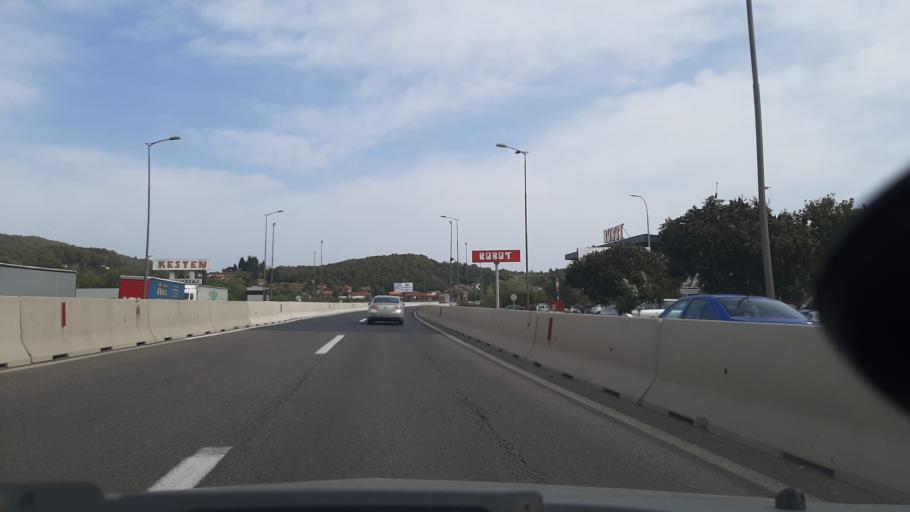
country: BA
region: Republika Srpska
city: Trn
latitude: 44.8696
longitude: 17.2537
